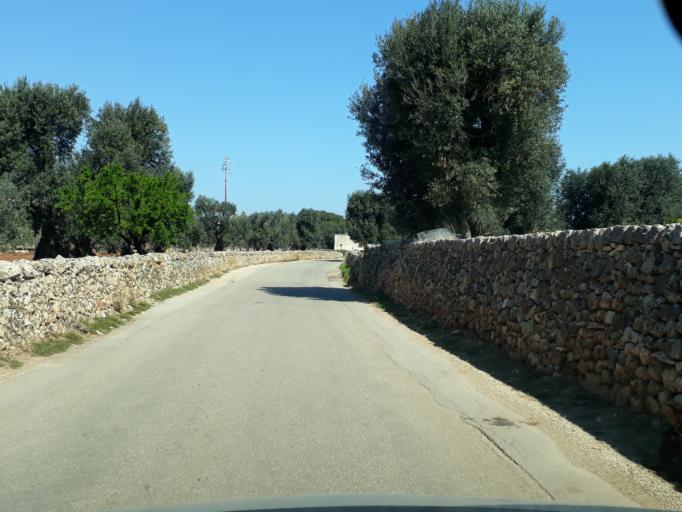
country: IT
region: Apulia
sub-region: Provincia di Brindisi
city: Fasano
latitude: 40.8338
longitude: 17.3784
